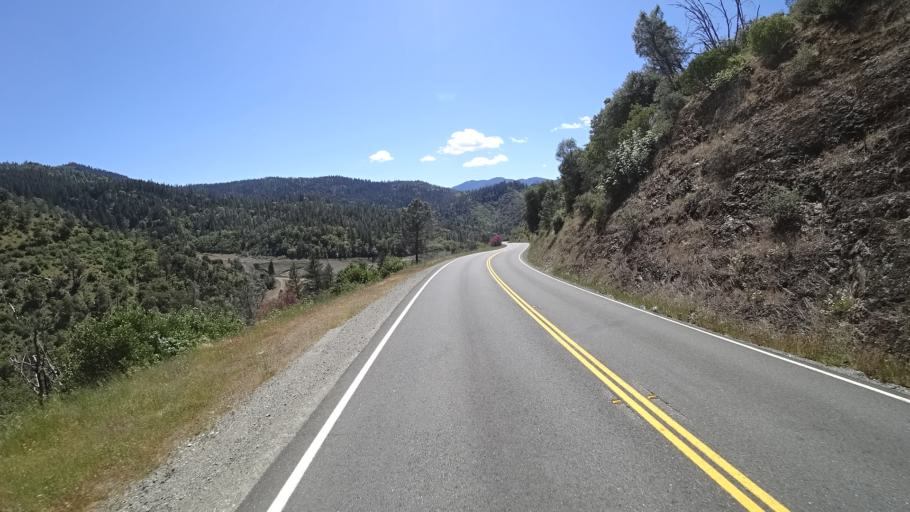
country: US
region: California
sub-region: Trinity County
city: Weaverville
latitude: 40.7372
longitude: -123.0075
